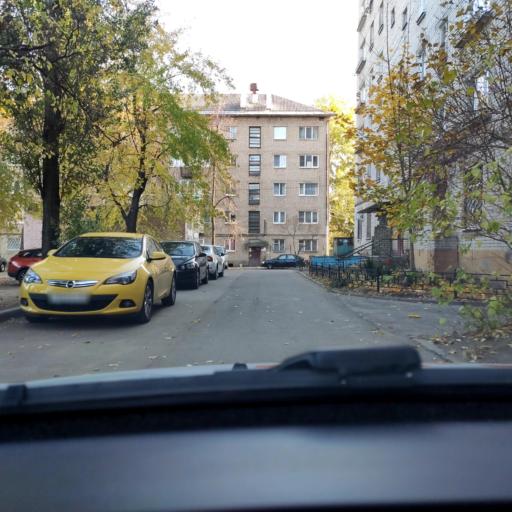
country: RU
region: Voronezj
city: Voronezh
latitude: 51.6463
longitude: 39.1658
